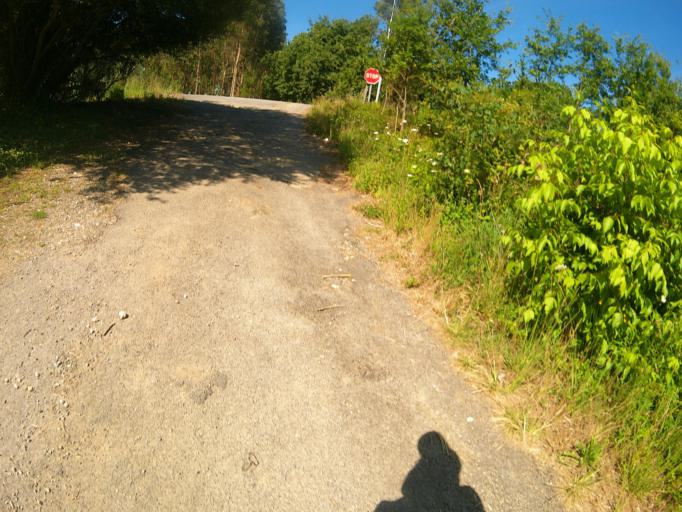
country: PT
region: Viana do Castelo
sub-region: Viana do Castelo
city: Darque
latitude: 41.7179
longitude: -8.6814
